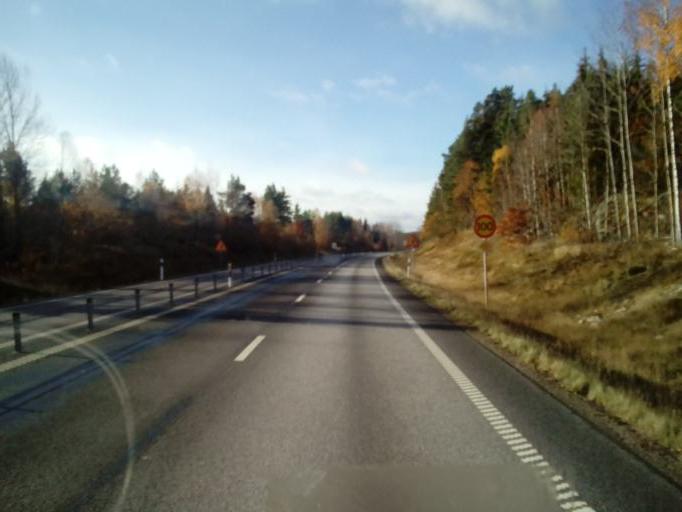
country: SE
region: Kalmar
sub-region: Vimmerby Kommun
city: Vimmerby
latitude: 57.7108
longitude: 16.0461
